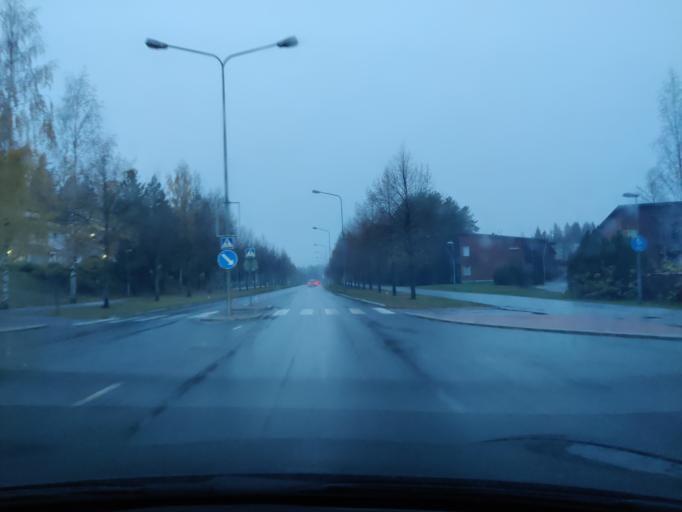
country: FI
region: Northern Savo
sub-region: Kuopio
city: Kuopio
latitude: 62.8348
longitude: 27.6640
